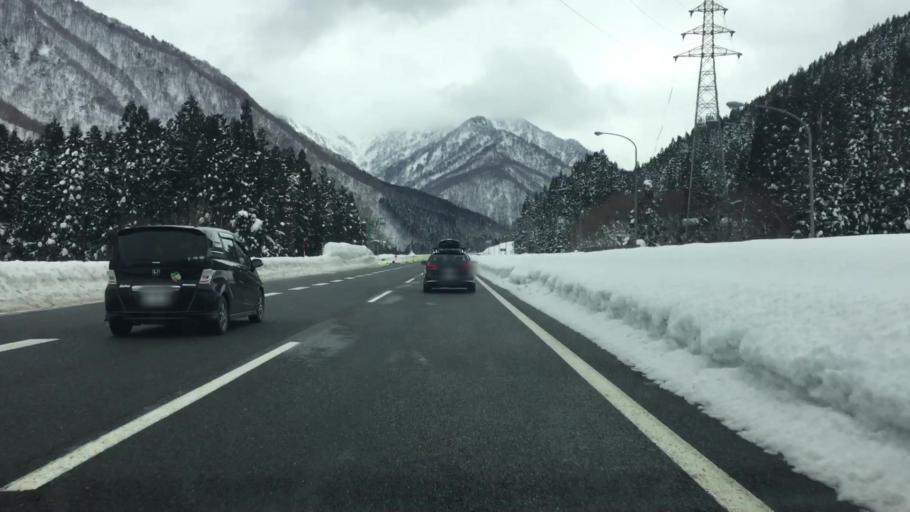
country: JP
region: Niigata
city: Shiozawa
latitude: 36.8802
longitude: 138.8556
